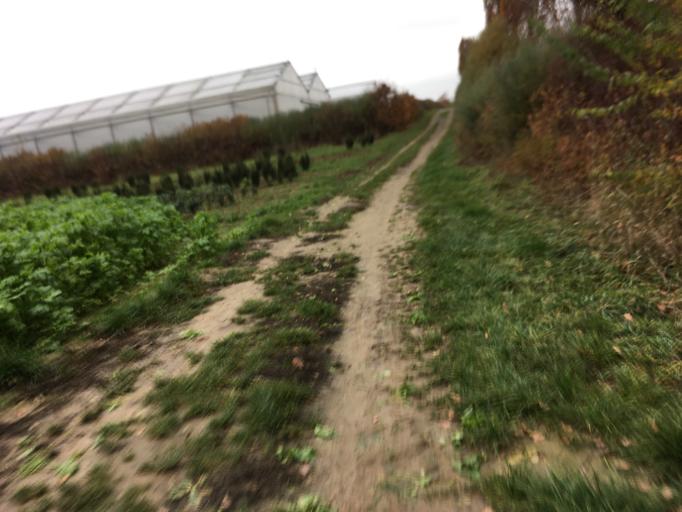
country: DE
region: Baden-Wuerttemberg
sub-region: Regierungsbezirk Stuttgart
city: Heilbronn
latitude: 49.1547
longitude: 9.1856
